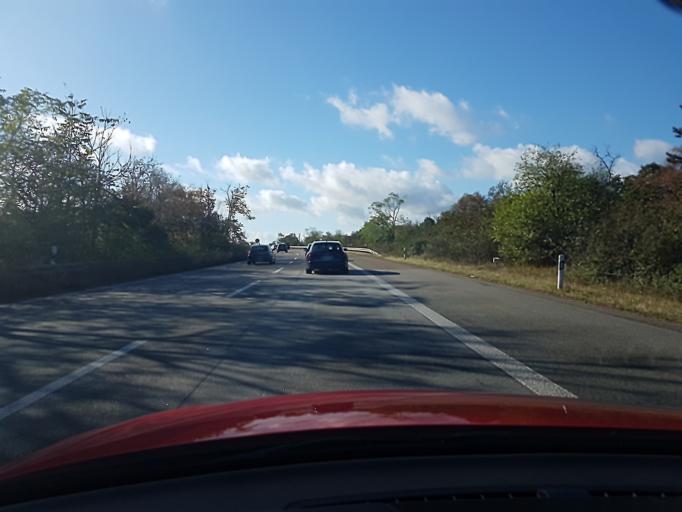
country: DE
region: Hesse
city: Griesheim
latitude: 49.8582
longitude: 8.5976
